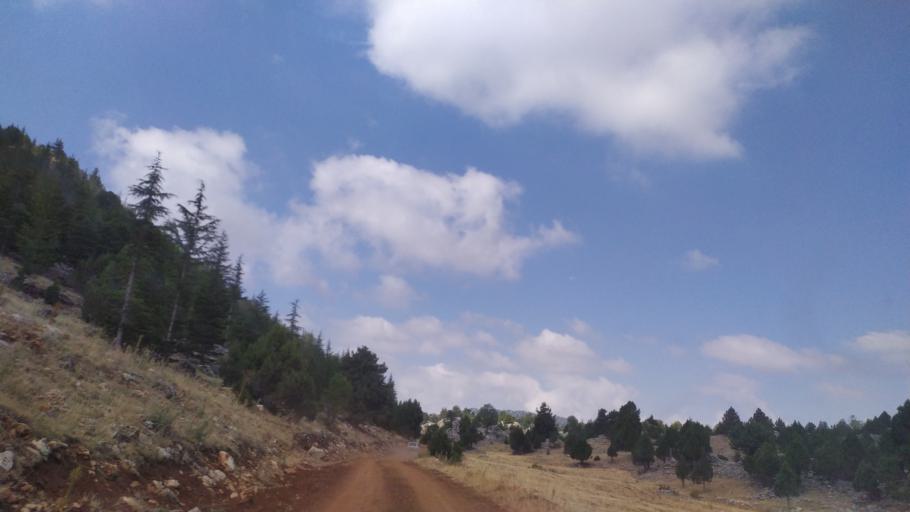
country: TR
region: Mersin
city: Kirobasi
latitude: 36.6208
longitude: 33.8434
